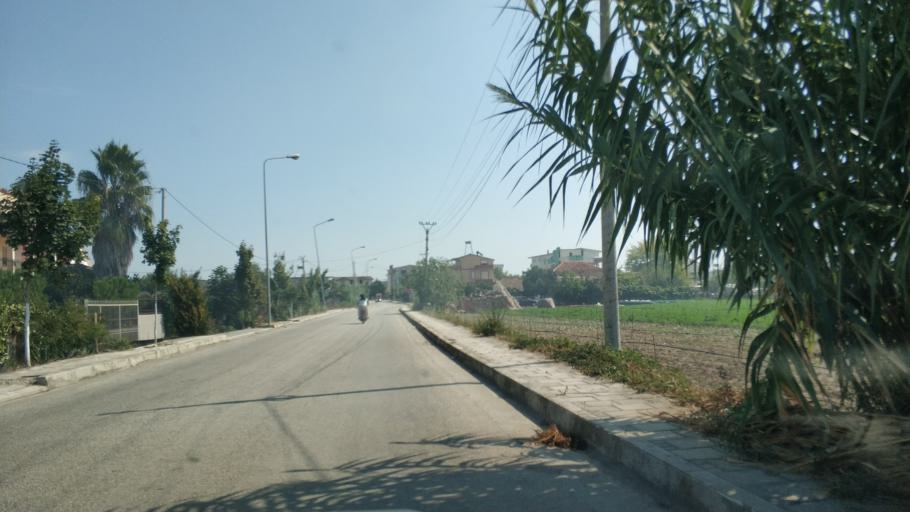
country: AL
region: Fier
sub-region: Rrethi i Lushnjes
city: Divjake
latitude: 41.0027
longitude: 19.5272
